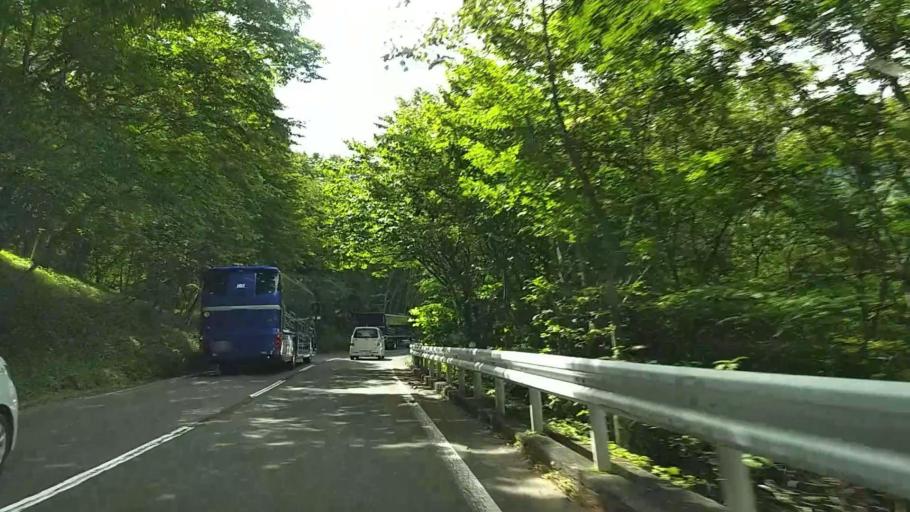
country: JP
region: Tochigi
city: Nikko
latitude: 36.7308
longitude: 139.5272
